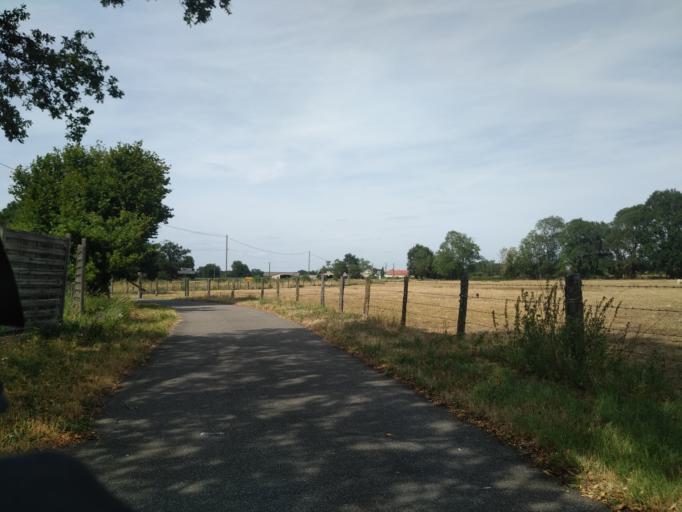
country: FR
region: Bourgogne
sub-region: Departement de Saone-et-Loire
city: Bourbon-Lancy
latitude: 46.5933
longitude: 3.7461
